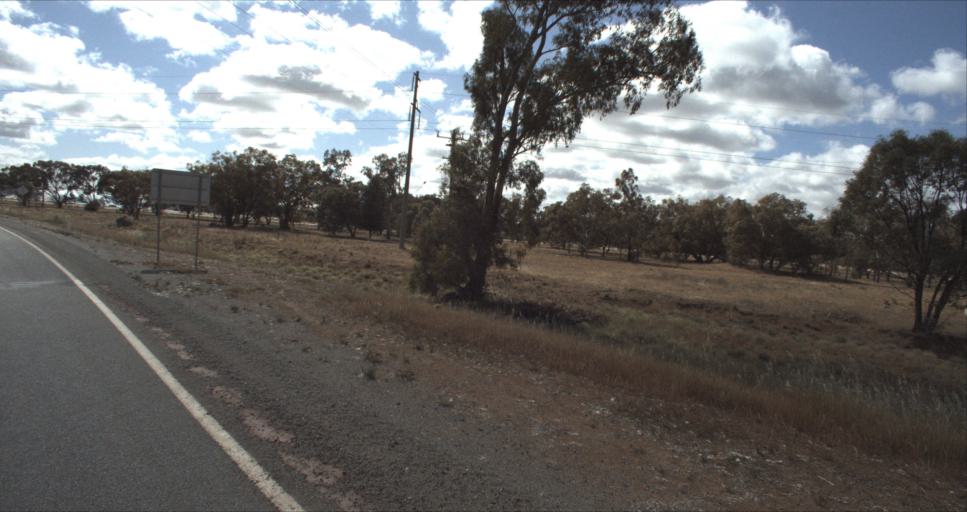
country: AU
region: New South Wales
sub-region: Murrumbidgee Shire
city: Darlington Point
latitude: -34.5971
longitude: 146.1614
